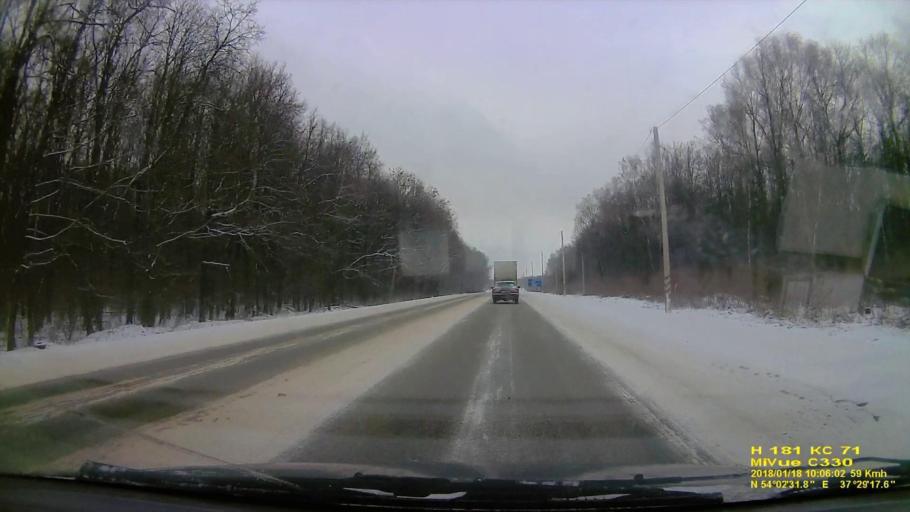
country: RU
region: Tula
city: Pervomayskiy
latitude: 54.0420
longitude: 37.4882
